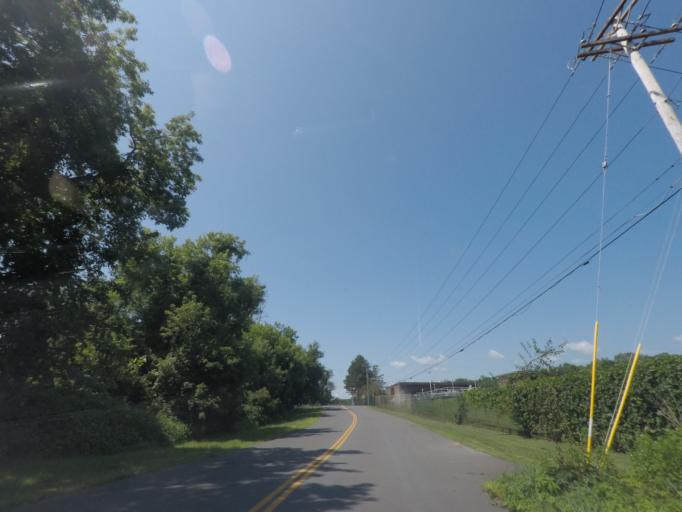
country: US
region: New York
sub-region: Saratoga County
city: Waterford
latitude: 42.7887
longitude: -73.6837
